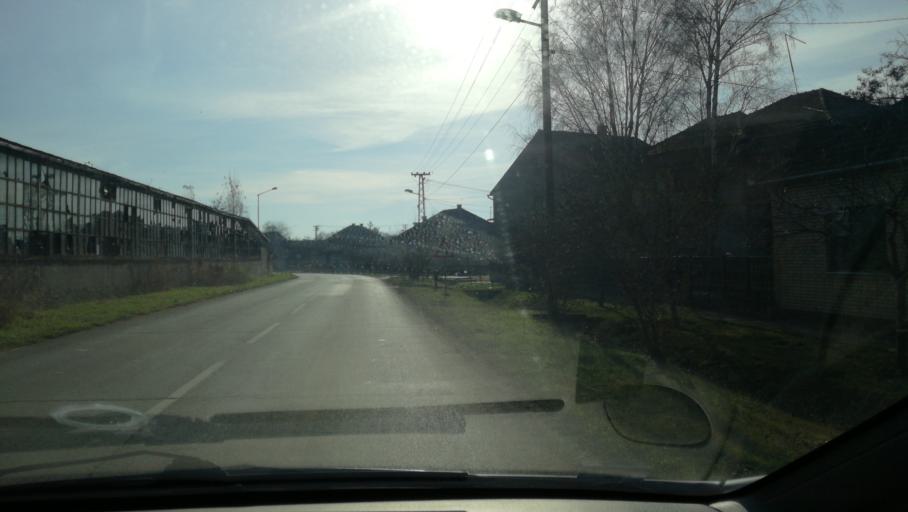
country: RS
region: Autonomna Pokrajina Vojvodina
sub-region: Severnobanatski Okrug
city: Kikinda
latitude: 45.8344
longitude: 20.4893
